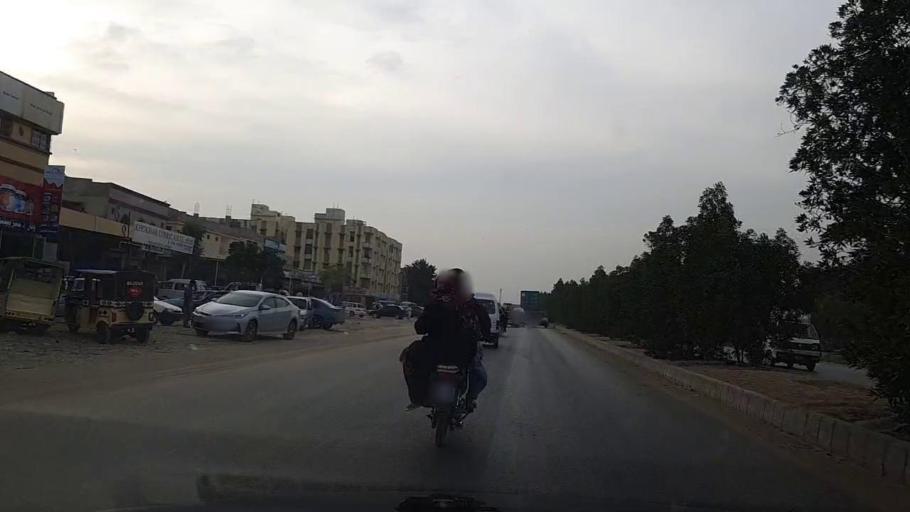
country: PK
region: Sindh
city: Malir Cantonment
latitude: 24.8600
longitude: 67.3344
